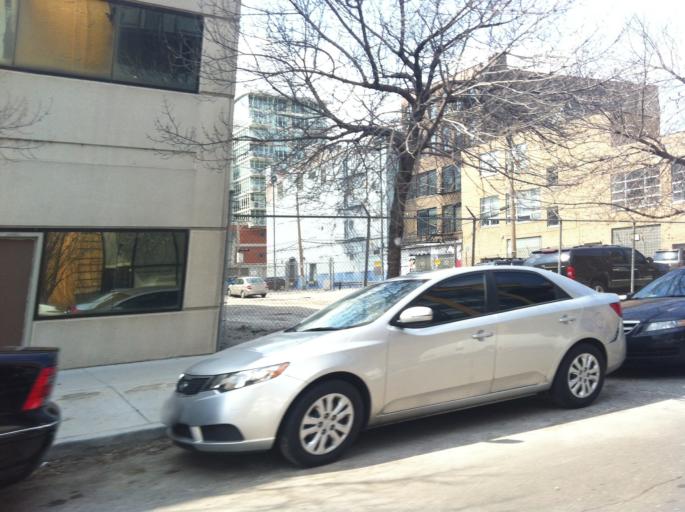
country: US
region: Illinois
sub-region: Cook County
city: Chicago
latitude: 41.8823
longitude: -87.6486
